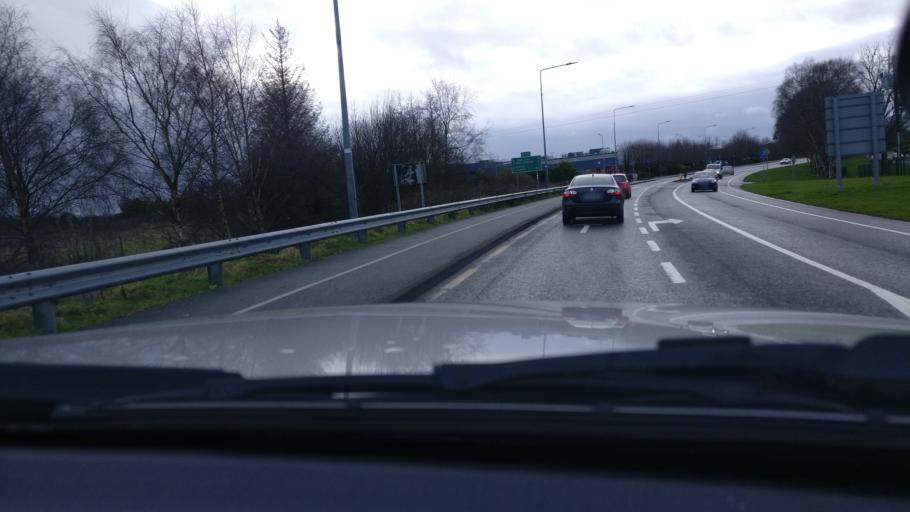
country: IE
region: Leinster
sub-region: An Iarmhi
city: Athlone
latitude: 53.4348
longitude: -7.9037
